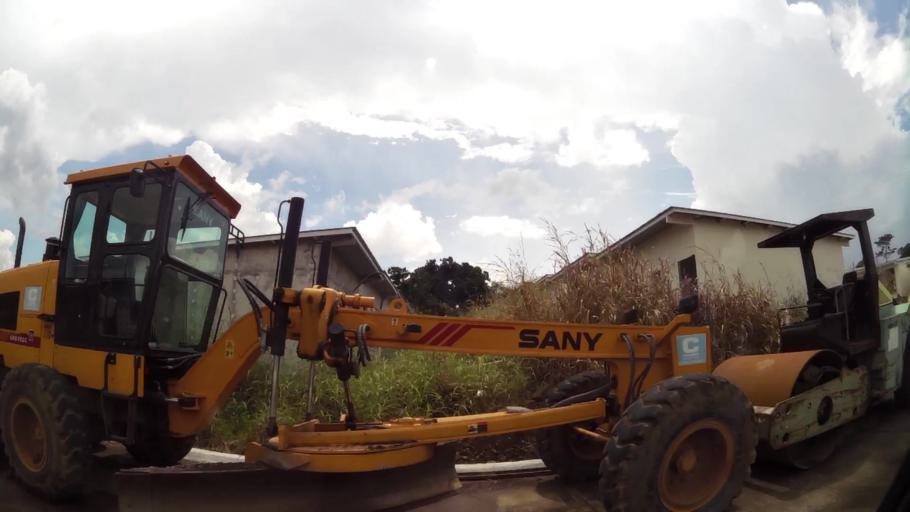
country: PA
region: Panama
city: Cabra Numero Uno
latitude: 9.1246
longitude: -79.3360
